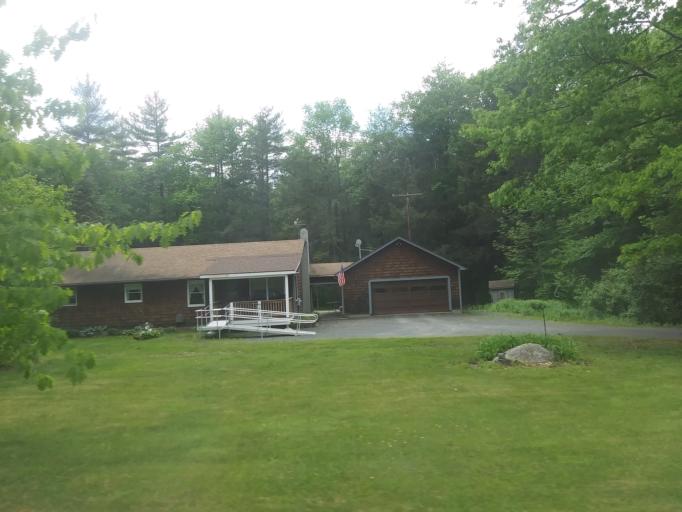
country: US
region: Massachusetts
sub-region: Franklin County
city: Shelburne Falls
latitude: 42.6048
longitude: -72.7608
